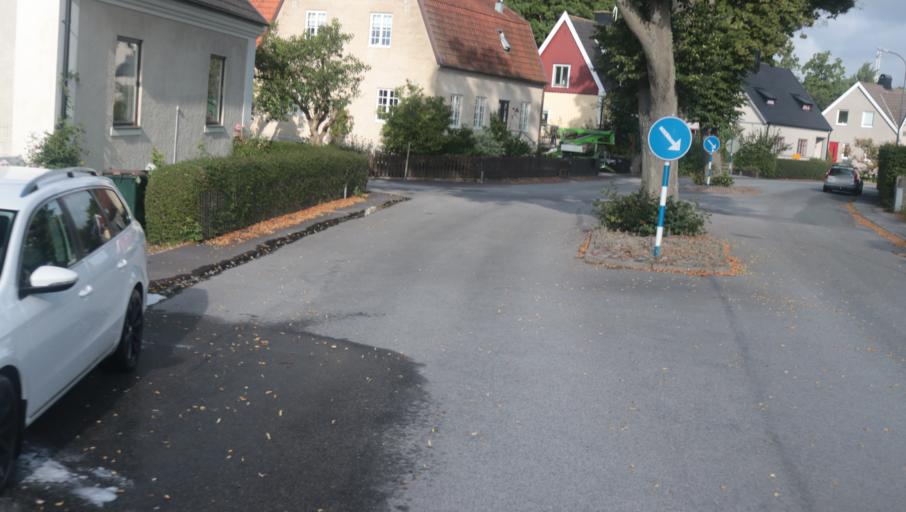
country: SE
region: Blekinge
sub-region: Karlshamns Kommun
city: Karlshamn
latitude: 56.1729
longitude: 14.8739
